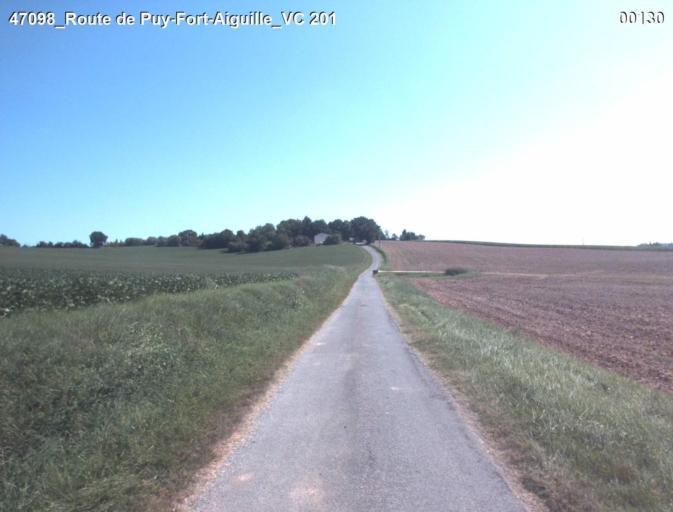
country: FR
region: Aquitaine
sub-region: Departement du Lot-et-Garonne
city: Nerac
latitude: 44.1036
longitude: 0.3960
